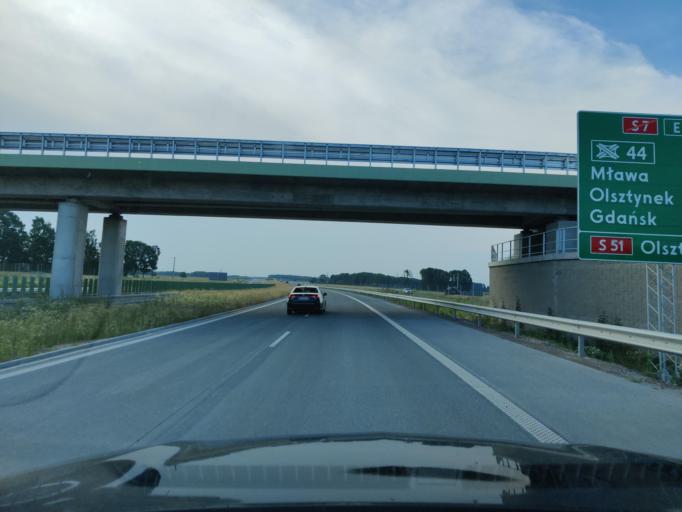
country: PL
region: Masovian Voivodeship
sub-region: Powiat mlawski
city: Strzegowo
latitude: 52.8643
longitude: 20.2865
